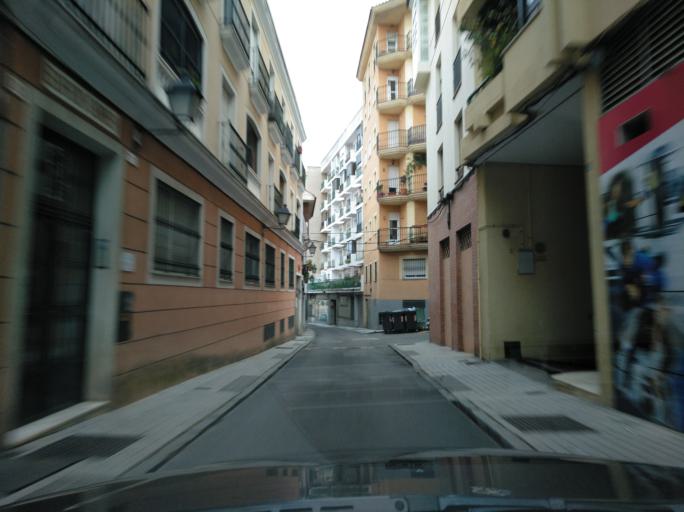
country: ES
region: Extremadura
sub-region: Provincia de Badajoz
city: Badajoz
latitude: 38.8778
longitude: -6.9659
